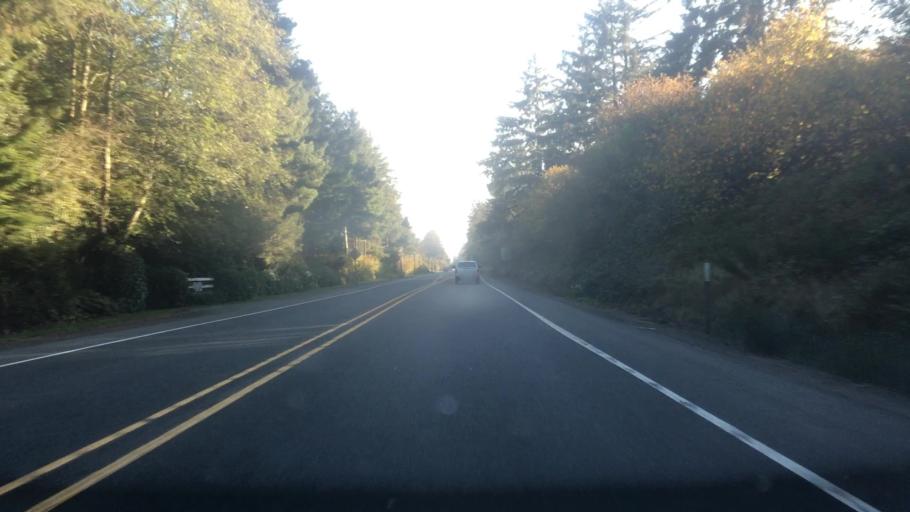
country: US
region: Oregon
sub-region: Clatsop County
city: Gearhart
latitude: 46.0628
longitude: -123.9158
